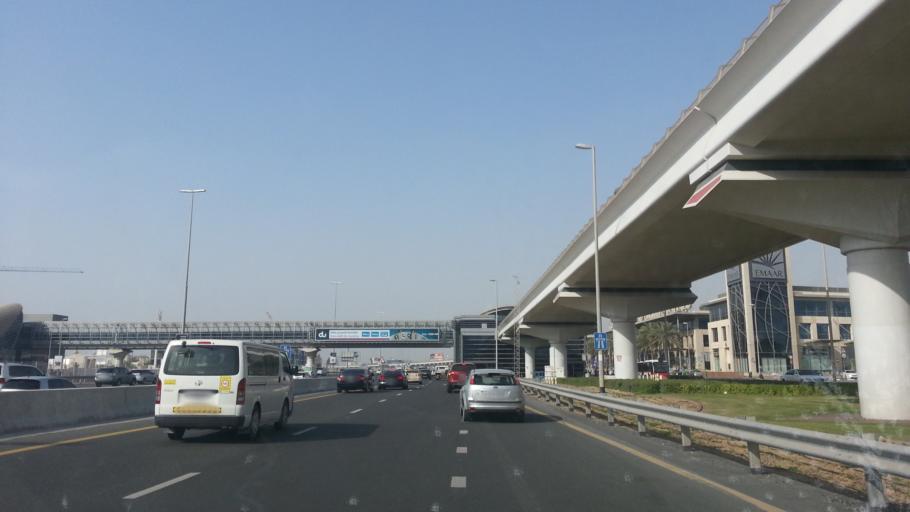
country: AE
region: Dubai
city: Dubai
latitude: 25.1253
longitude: 55.2057
